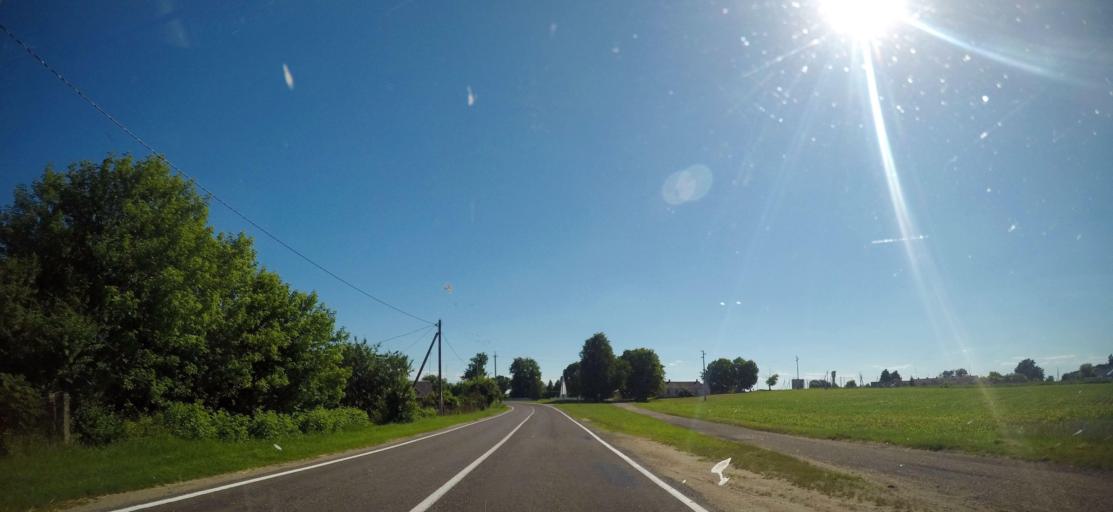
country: BY
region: Grodnenskaya
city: Vyalikaya Byerastavitsa
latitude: 53.1620
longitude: 23.9867
